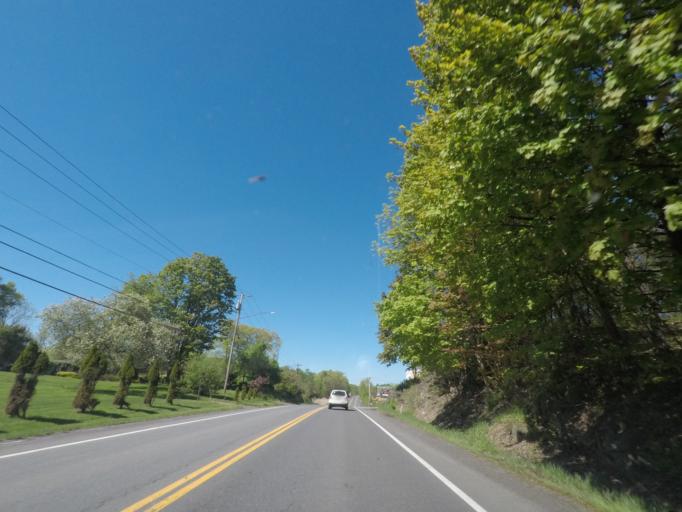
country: US
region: New York
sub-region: Greene County
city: Jefferson Heights
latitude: 42.2367
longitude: -73.8676
